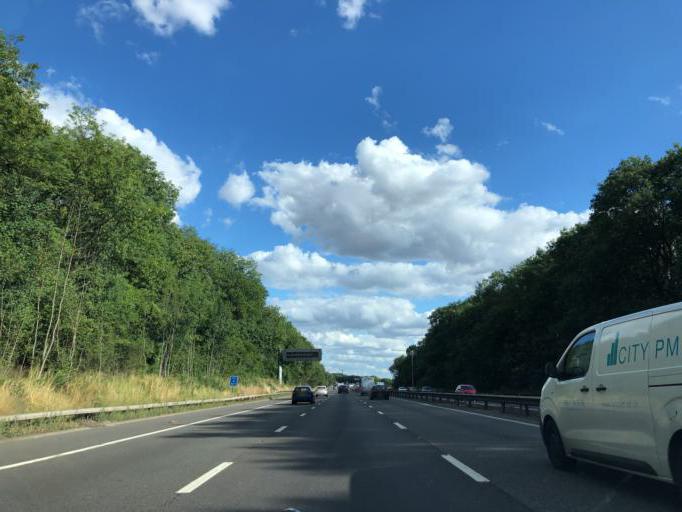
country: GB
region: England
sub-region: Northamptonshire
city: Hartwell
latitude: 52.1450
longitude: -0.8384
